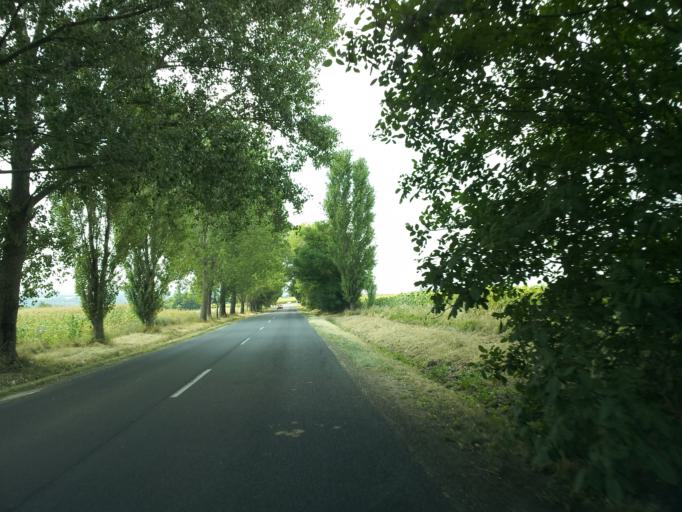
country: HU
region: Gyor-Moson-Sopron
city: Pannonhalma
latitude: 47.5605
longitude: 17.7331
